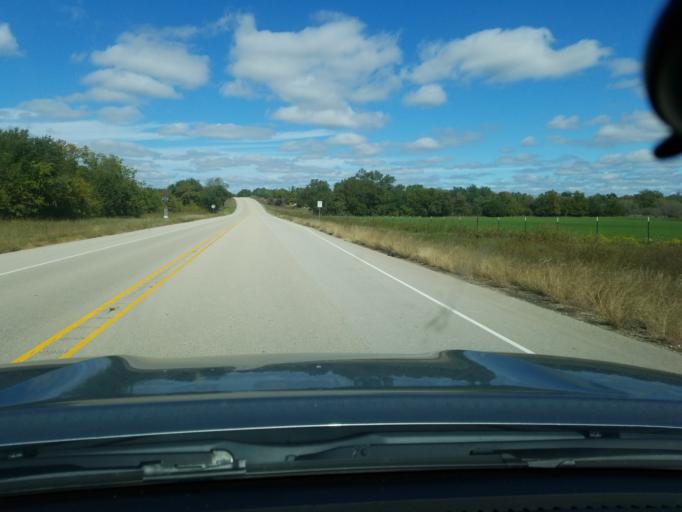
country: US
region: Texas
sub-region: Hamilton County
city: Hamilton
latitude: 31.5835
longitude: -98.1570
